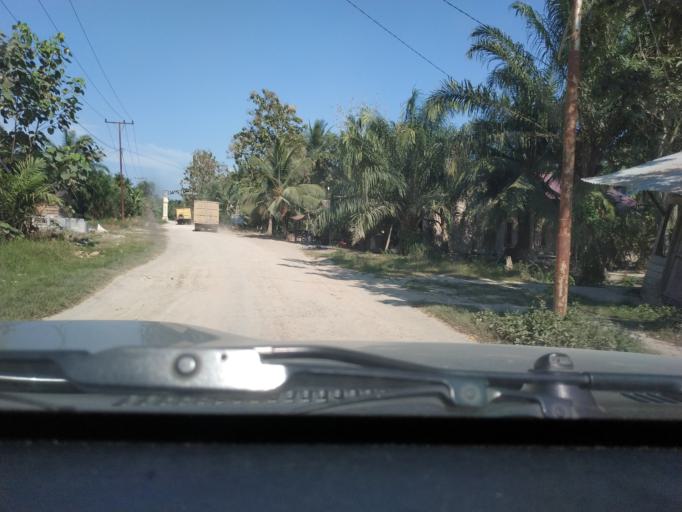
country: ID
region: North Sumatra
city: Tanjungbalai
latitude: 2.8369
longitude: 99.9650
